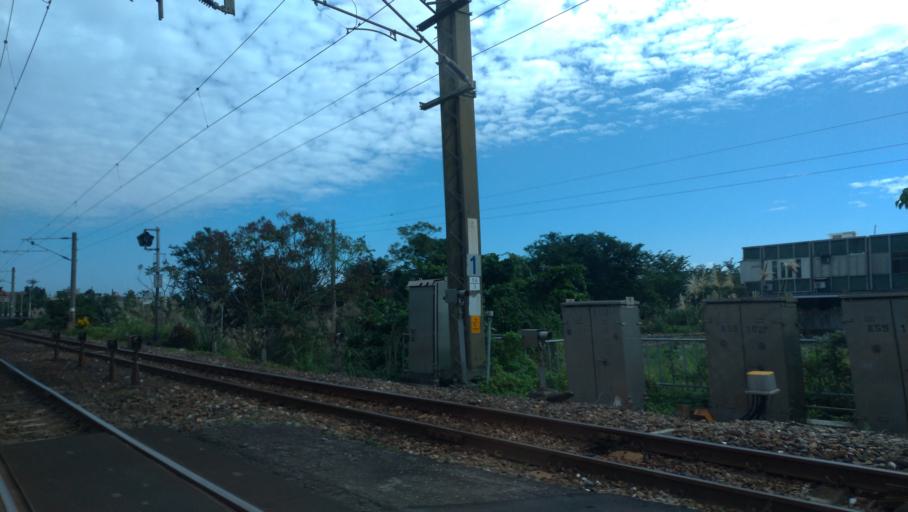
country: TW
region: Taiwan
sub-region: Yilan
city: Yilan
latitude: 24.8424
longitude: 121.8068
